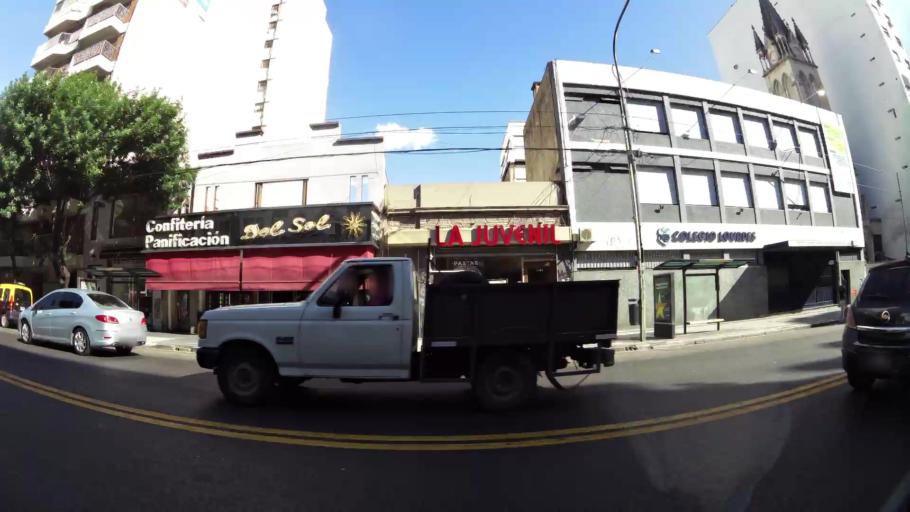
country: AR
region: Buenos Aires F.D.
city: Villa Santa Rita
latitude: -34.6260
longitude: -58.4549
